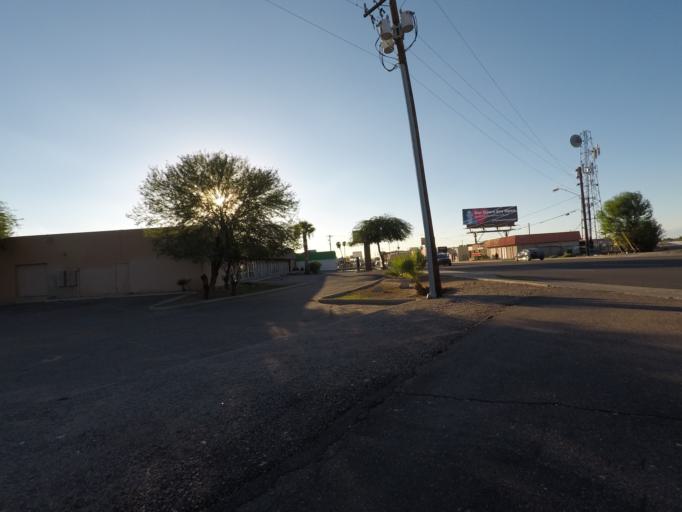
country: US
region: Arizona
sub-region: Maricopa County
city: Phoenix
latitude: 33.4656
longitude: -112.0161
